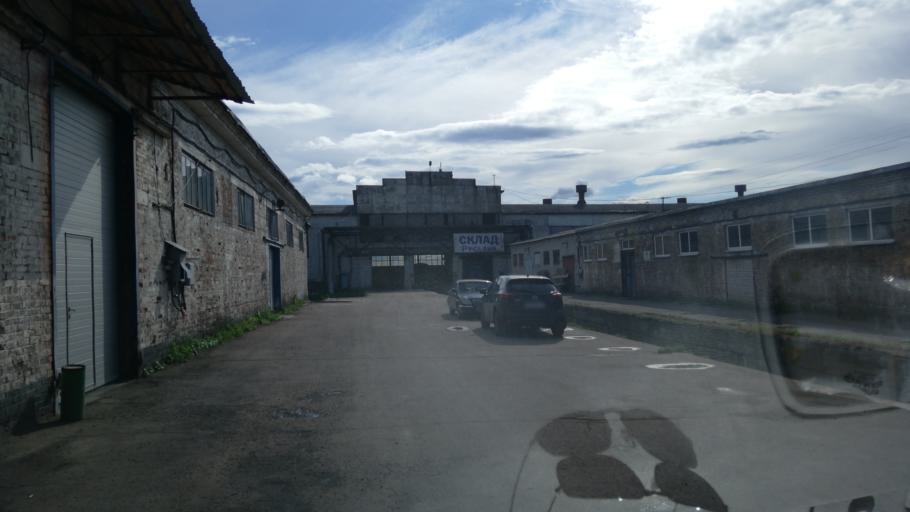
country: RU
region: Jaroslavl
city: Yaroslavl
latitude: 57.6257
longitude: 39.8220
